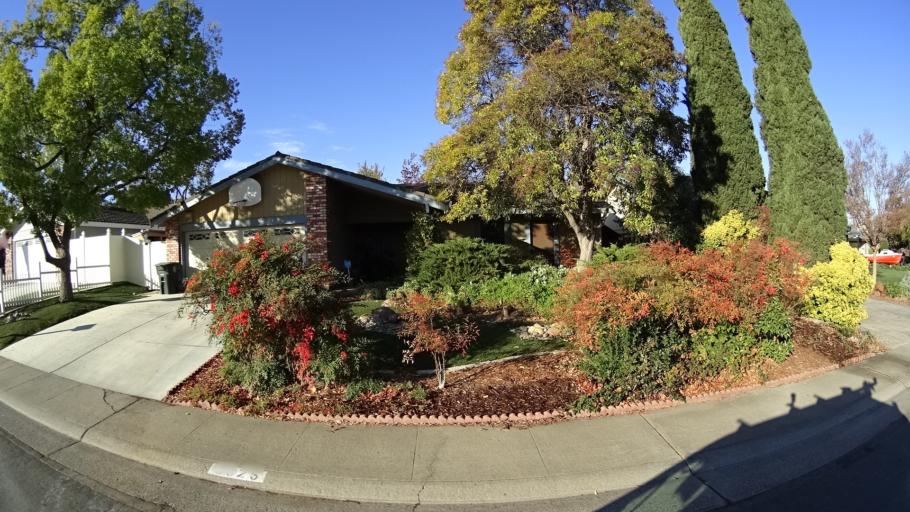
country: US
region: California
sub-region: Sacramento County
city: Citrus Heights
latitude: 38.6723
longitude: -121.3026
